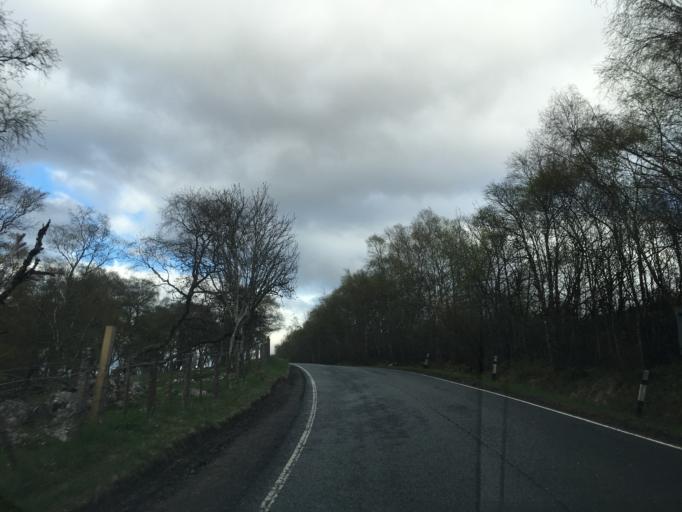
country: GB
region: Scotland
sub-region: Highland
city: Kingussie
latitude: 57.0072
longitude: -4.2600
